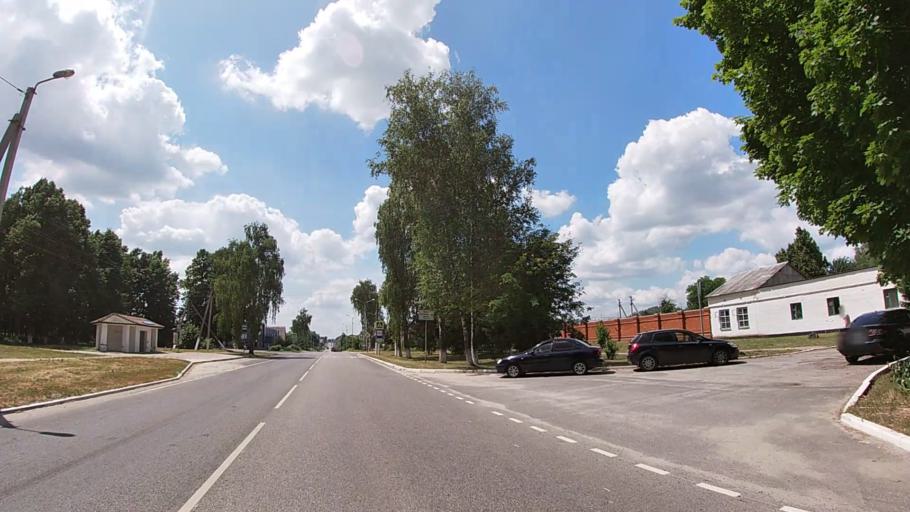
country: RU
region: Belgorod
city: Grayvoron
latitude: 50.4861
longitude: 35.6899
